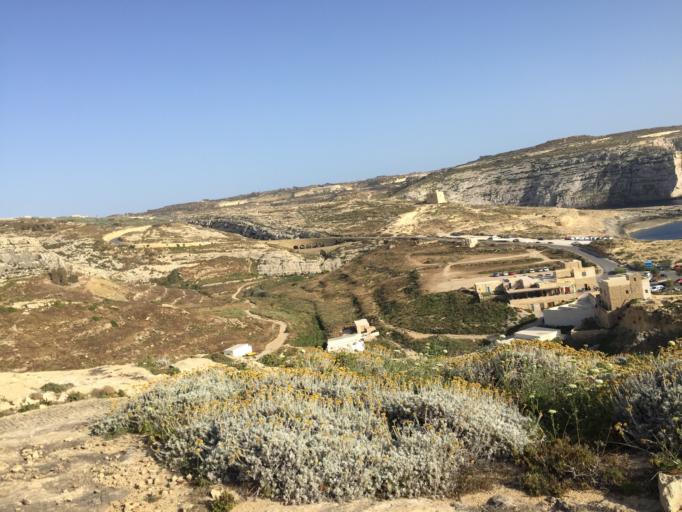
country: MT
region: Saint Lawrence
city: San Lawrenz
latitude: 36.0542
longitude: 14.1903
